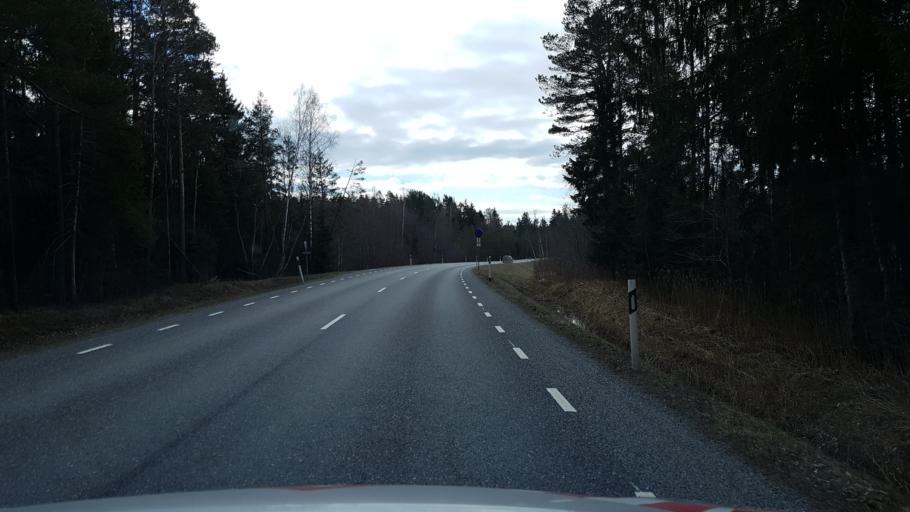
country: EE
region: Laeaene-Virumaa
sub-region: Rakke vald
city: Rakke
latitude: 59.0399
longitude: 26.2399
